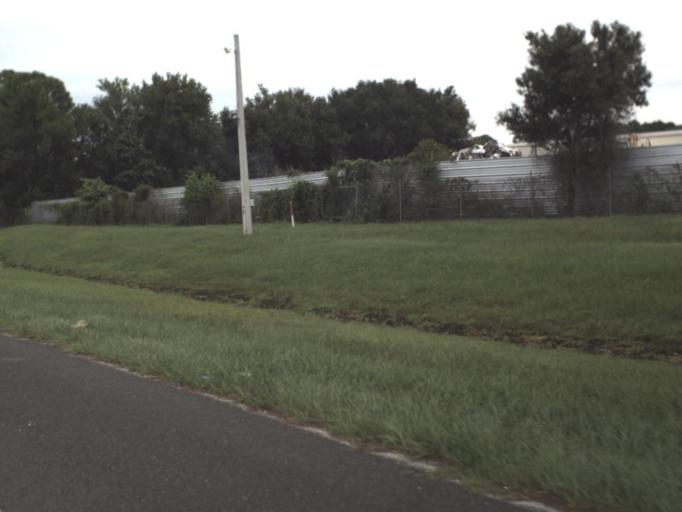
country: US
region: Florida
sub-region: Manatee County
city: Whitfield
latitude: 27.4209
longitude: -82.5326
